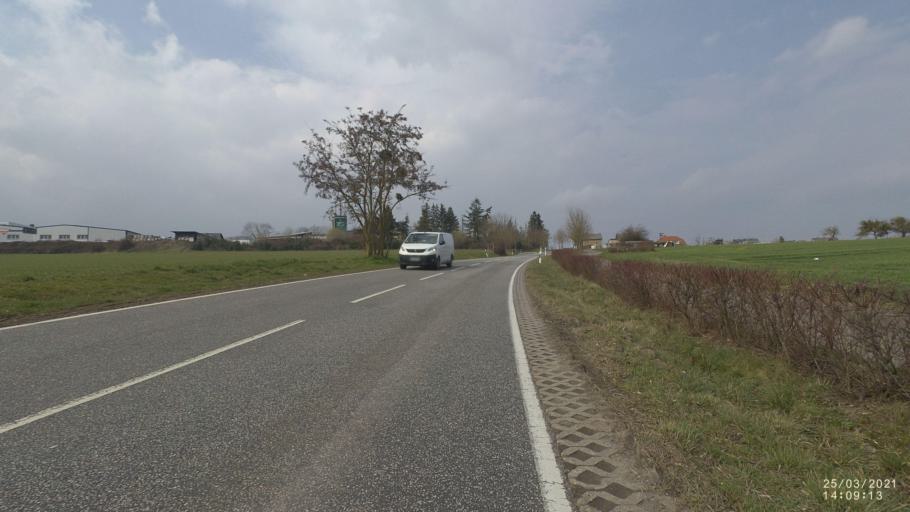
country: DE
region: Rheinland-Pfalz
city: Ettringen
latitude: 50.3490
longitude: 7.2228
